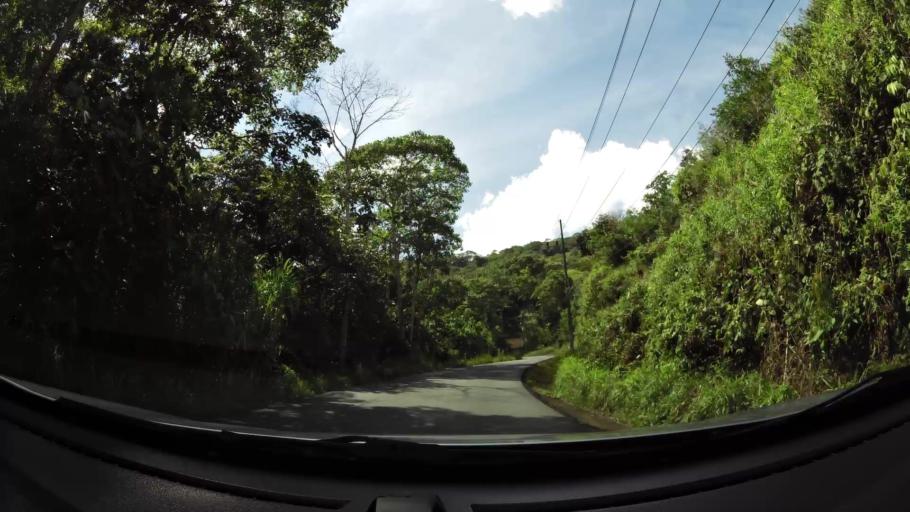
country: CR
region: San Jose
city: San Isidro
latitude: 9.3401
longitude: -83.7366
